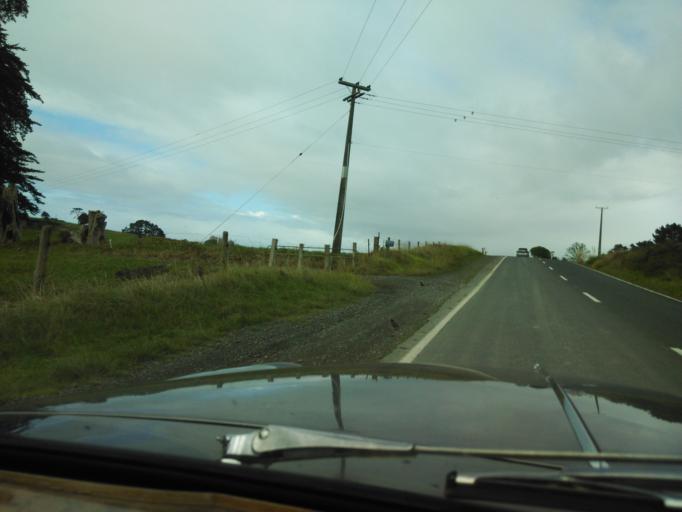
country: NZ
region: Auckland
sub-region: Auckland
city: Wellsford
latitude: -36.3329
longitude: 174.3941
